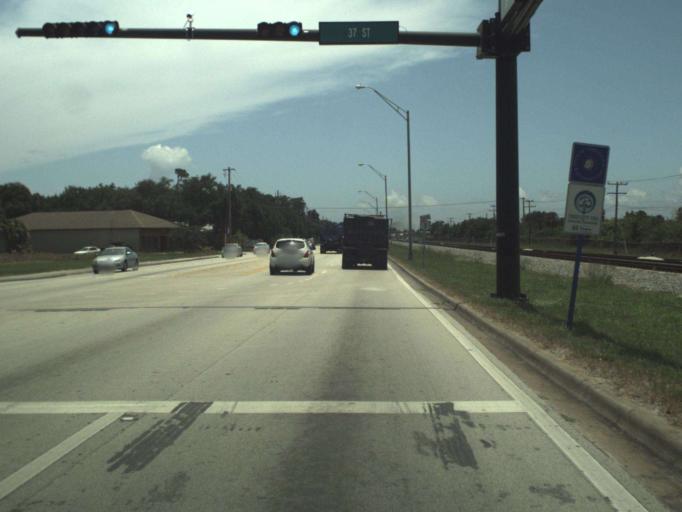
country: US
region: Florida
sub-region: Indian River County
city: Gifford
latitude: 27.6604
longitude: -80.4043
